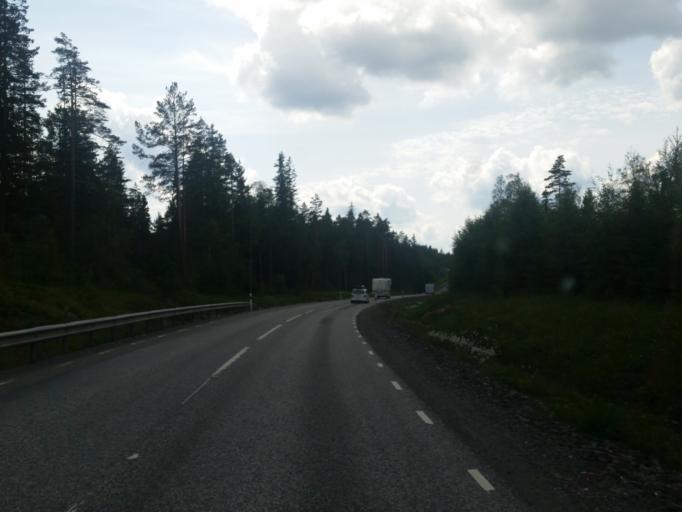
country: SE
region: OErebro
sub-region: Ljusnarsbergs Kommun
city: Kopparberg
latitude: 59.9378
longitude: 15.0263
